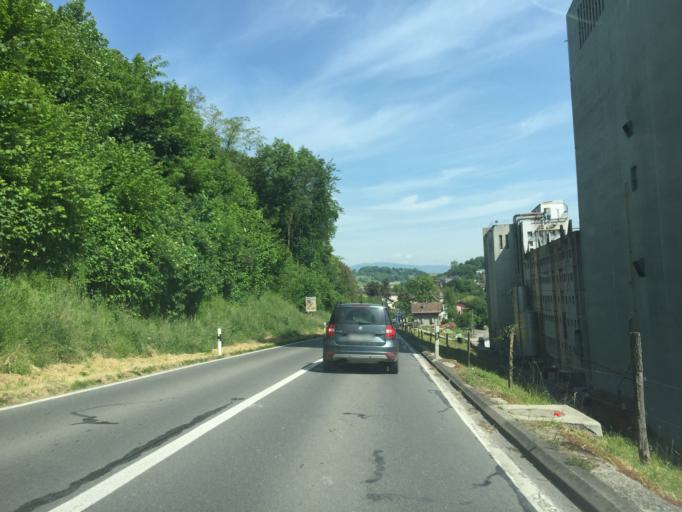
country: CH
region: Vaud
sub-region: Gros-de-Vaud District
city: Penthalaz
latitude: 46.6038
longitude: 6.5227
